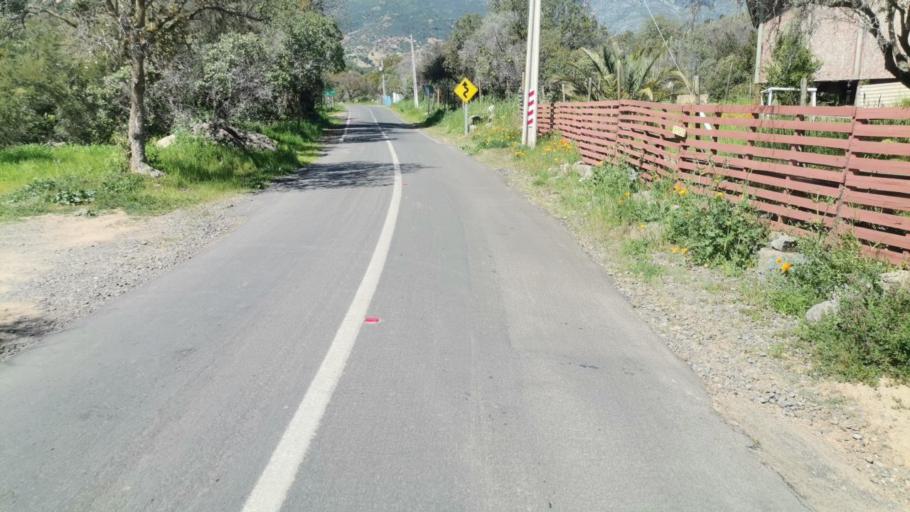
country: CL
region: Valparaiso
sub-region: Provincia de Marga Marga
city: Limache
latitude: -33.1833
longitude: -71.1095
